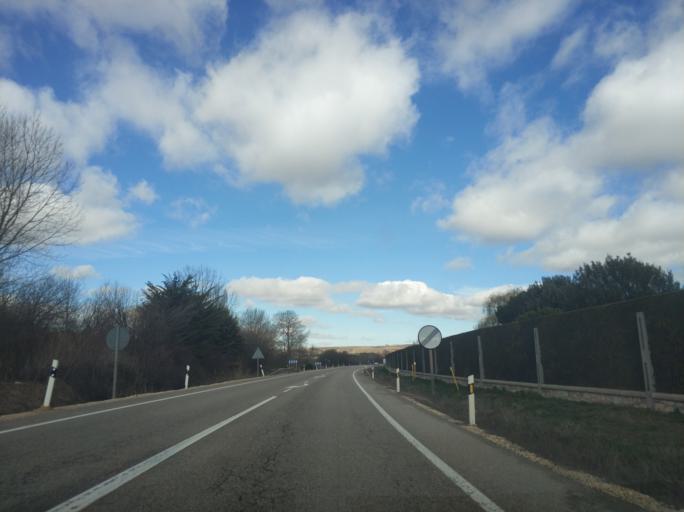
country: ES
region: Castille and Leon
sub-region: Provincia de Burgos
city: Sarracin
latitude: 42.2541
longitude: -3.6897
